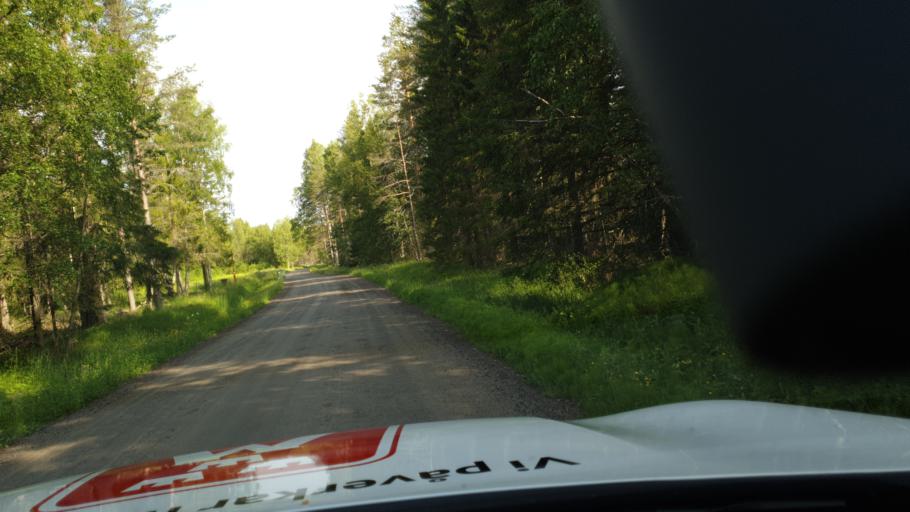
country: SE
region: Vaesterbotten
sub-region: Robertsfors Kommun
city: Robertsfors
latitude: 64.2186
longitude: 21.0730
